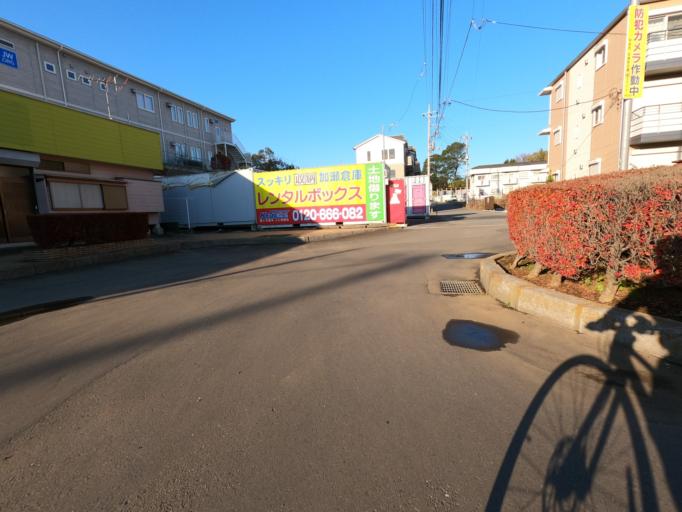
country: JP
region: Ibaraki
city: Moriya
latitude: 35.9347
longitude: 140.0021
